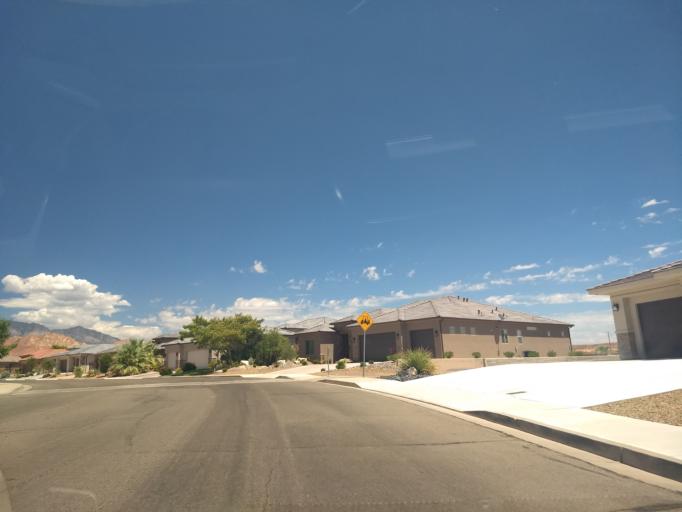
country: US
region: Utah
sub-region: Washington County
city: Washington
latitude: 37.1478
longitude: -113.5206
